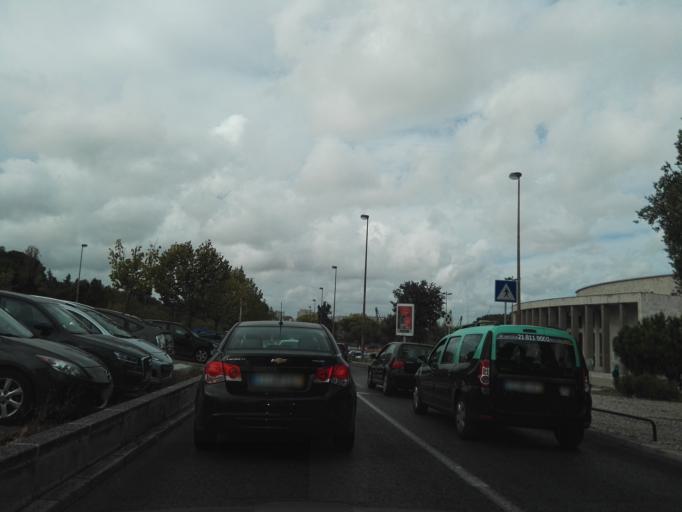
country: PT
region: Lisbon
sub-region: Odivelas
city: Olival do Basto
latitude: 38.7515
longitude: -9.1588
